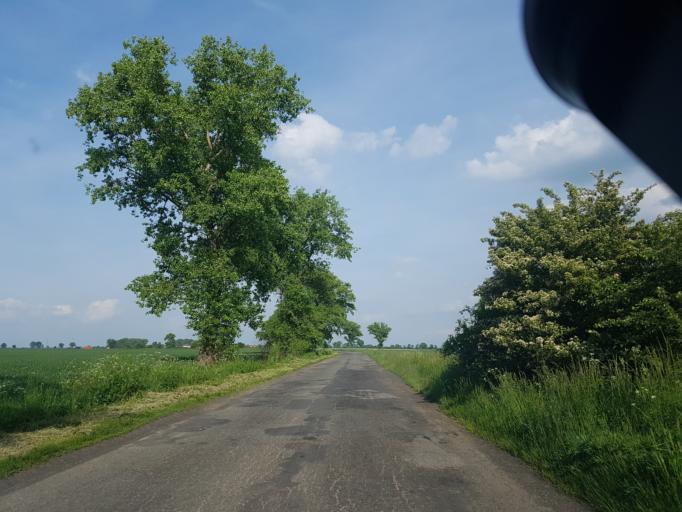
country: PL
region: Lower Silesian Voivodeship
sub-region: Powiat strzelinski
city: Wiazow
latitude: 50.8650
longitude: 17.1694
